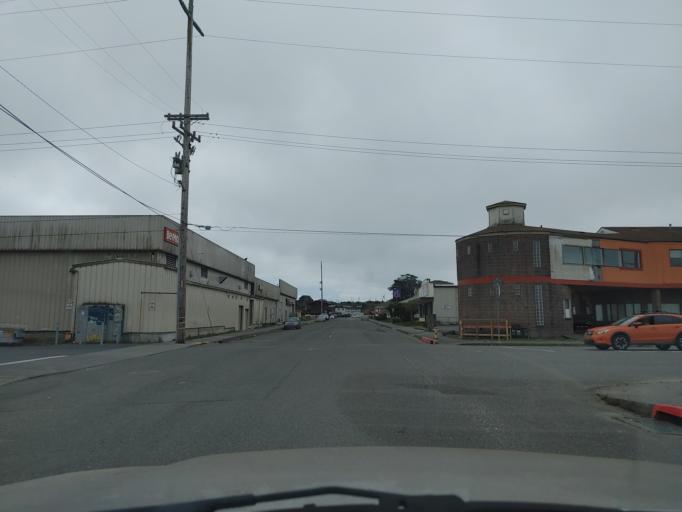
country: US
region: California
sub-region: Humboldt County
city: Eureka
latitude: 40.7931
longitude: -124.1791
